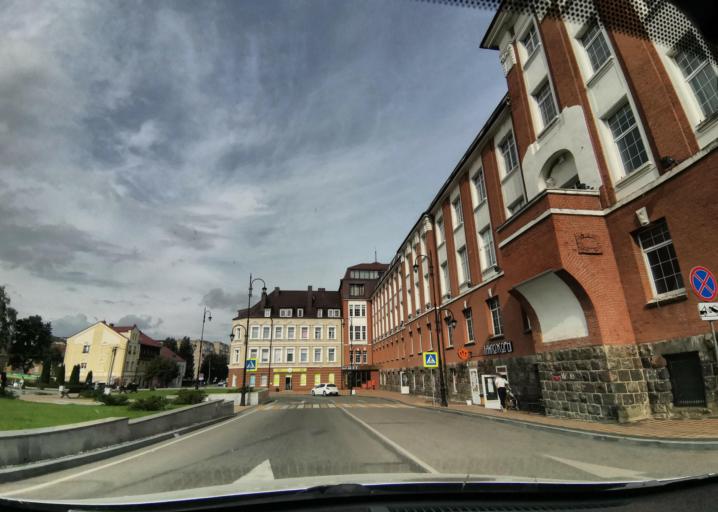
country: RU
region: Kaliningrad
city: Gusev
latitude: 54.5918
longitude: 22.2017
